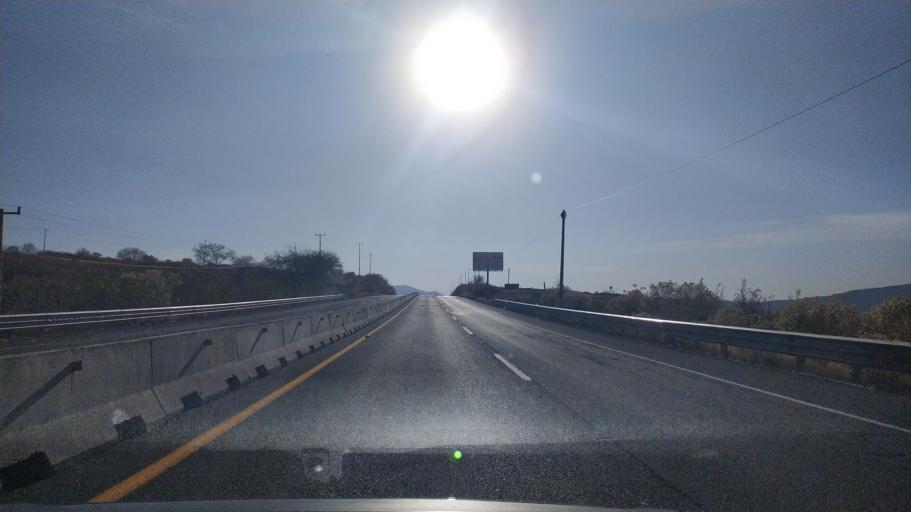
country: MX
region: Jalisco
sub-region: Poncitlan
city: Cuitzeo (La Estancia)
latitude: 20.3652
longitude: -102.8172
